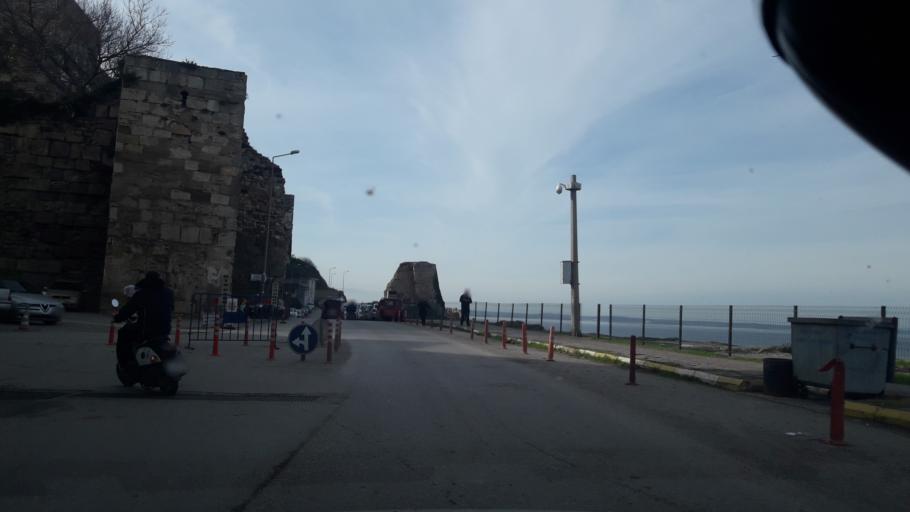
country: TR
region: Sinop
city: Sinop
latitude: 42.0264
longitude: 35.1438
